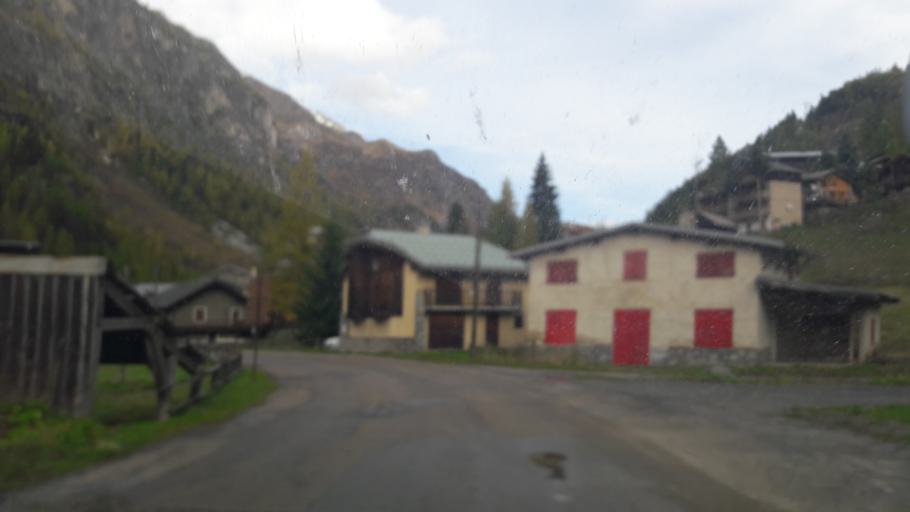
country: FR
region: Rhone-Alpes
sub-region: Departement de la Savoie
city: Tignes
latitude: 45.5067
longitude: 6.9217
